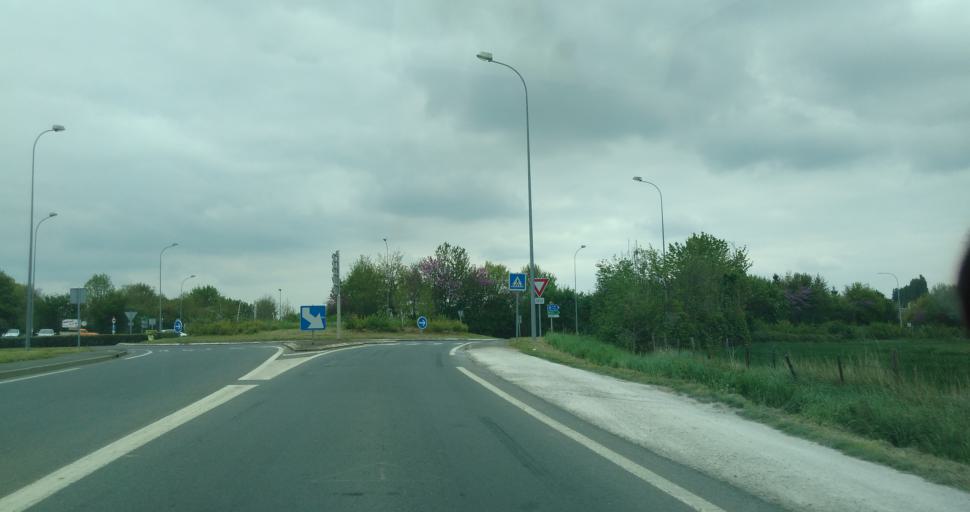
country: FR
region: Poitou-Charentes
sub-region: Departement des Deux-Sevres
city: Champdeniers-Saint-Denis
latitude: 46.4689
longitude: -0.3687
